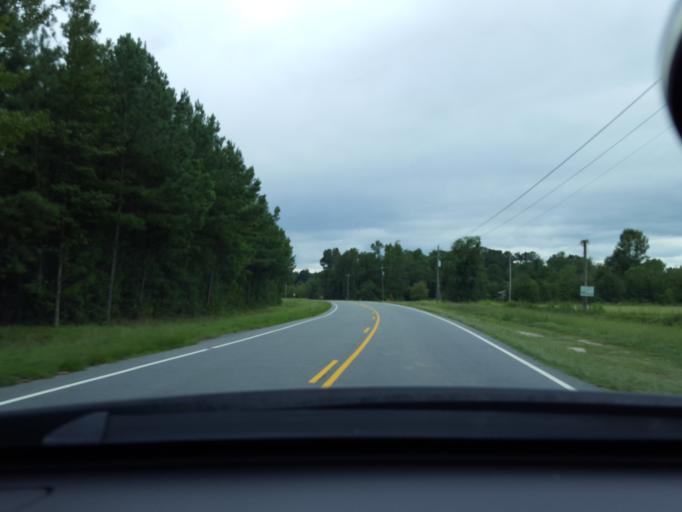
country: US
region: North Carolina
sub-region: Sampson County
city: Roseboro
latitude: 34.7571
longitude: -78.4149
